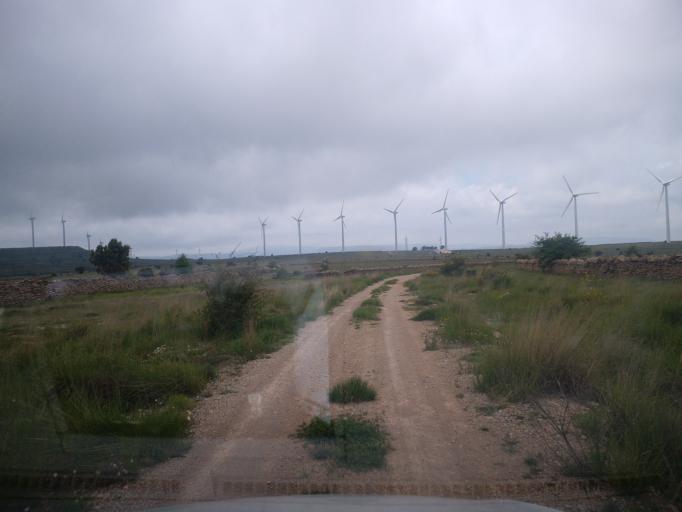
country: ES
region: Valencia
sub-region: Provincia de Castello
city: Castellfort
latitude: 40.4666
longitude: -0.2010
